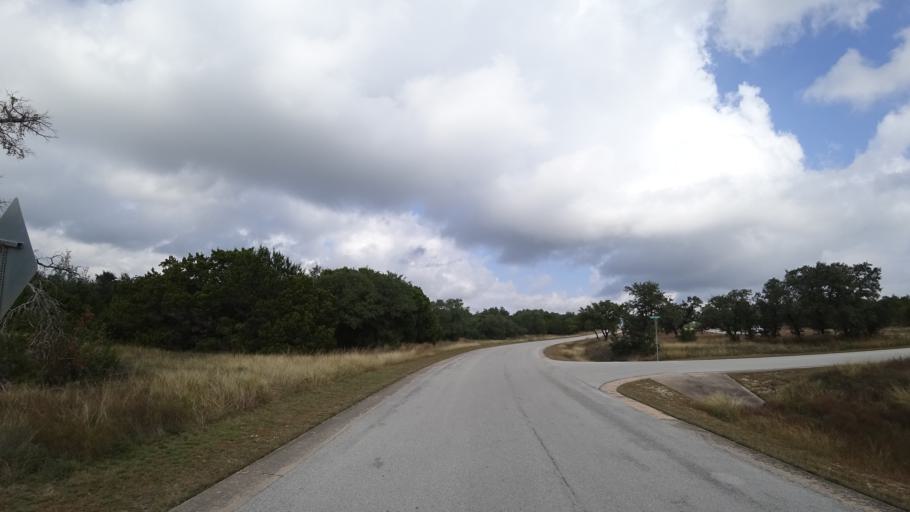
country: US
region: Texas
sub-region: Travis County
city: Barton Creek
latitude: 30.2996
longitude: -97.8919
